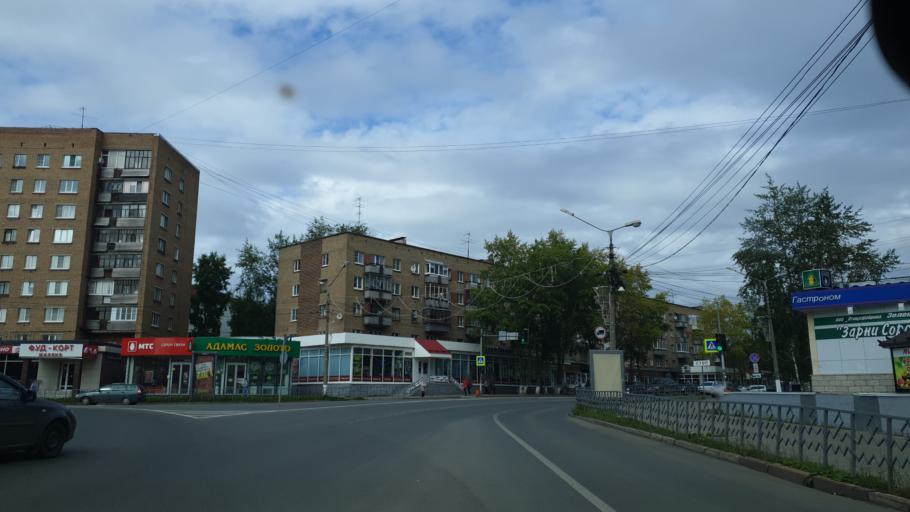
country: RU
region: Komi Republic
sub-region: Syktyvdinskiy Rayon
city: Syktyvkar
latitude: 61.6637
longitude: 50.8166
